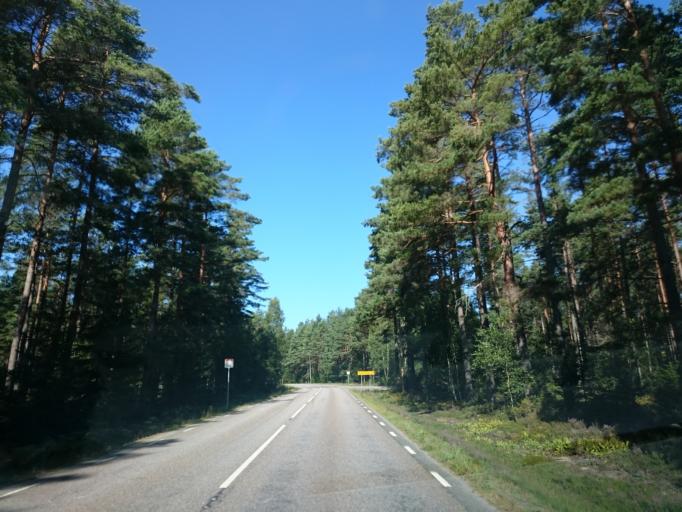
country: SE
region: OEstergoetland
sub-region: Norrkopings Kommun
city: Krokek
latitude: 58.6549
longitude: 16.5338
